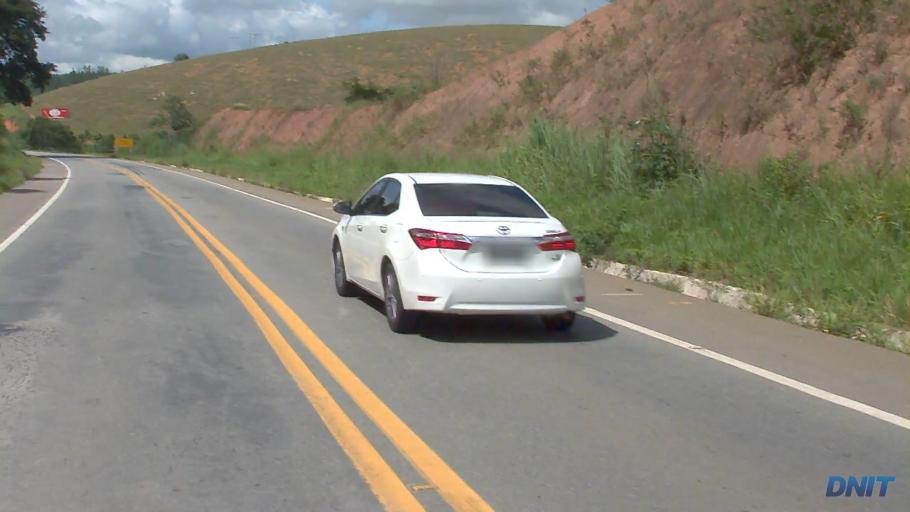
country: BR
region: Minas Gerais
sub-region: Belo Oriente
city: Belo Oriente
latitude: -19.1107
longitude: -42.2030
